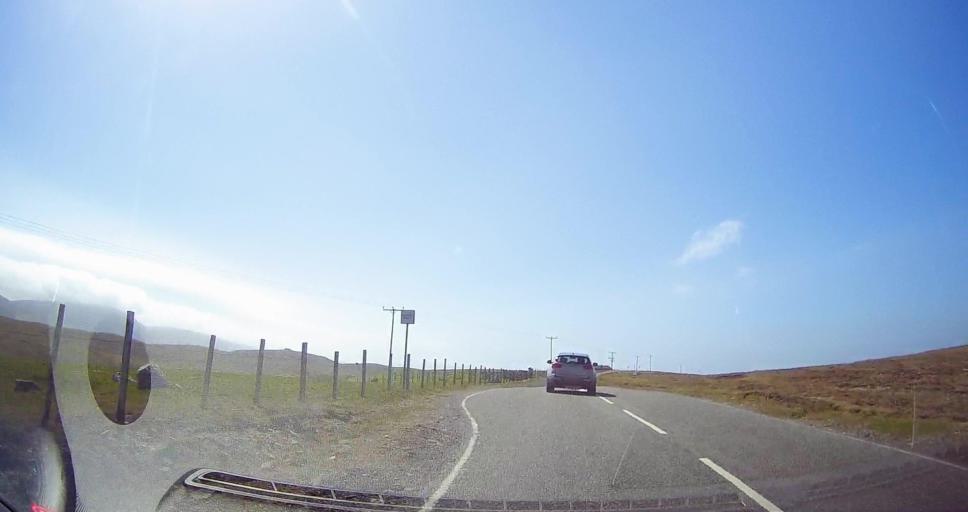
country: GB
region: Scotland
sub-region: Shetland Islands
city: Sandwick
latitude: 60.0924
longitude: -1.3240
